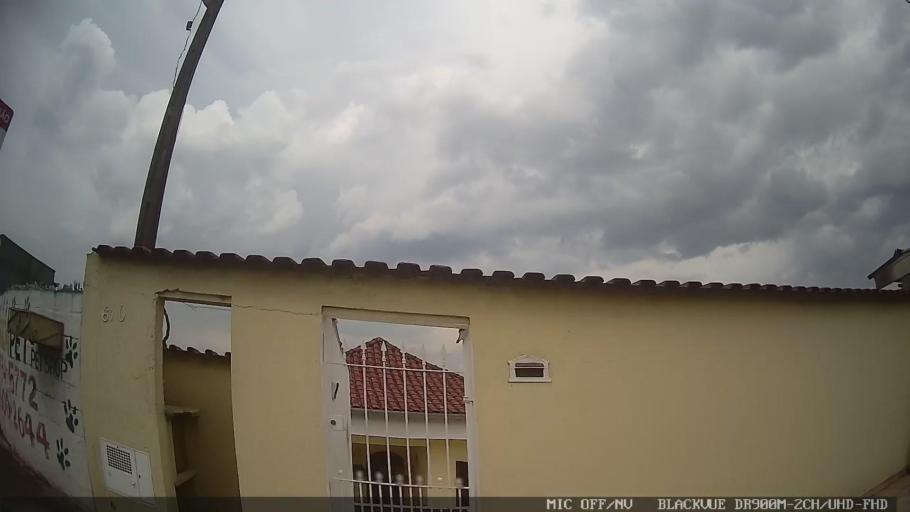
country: BR
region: Sao Paulo
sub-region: Aruja
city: Aruja
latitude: -23.4441
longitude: -46.3189
